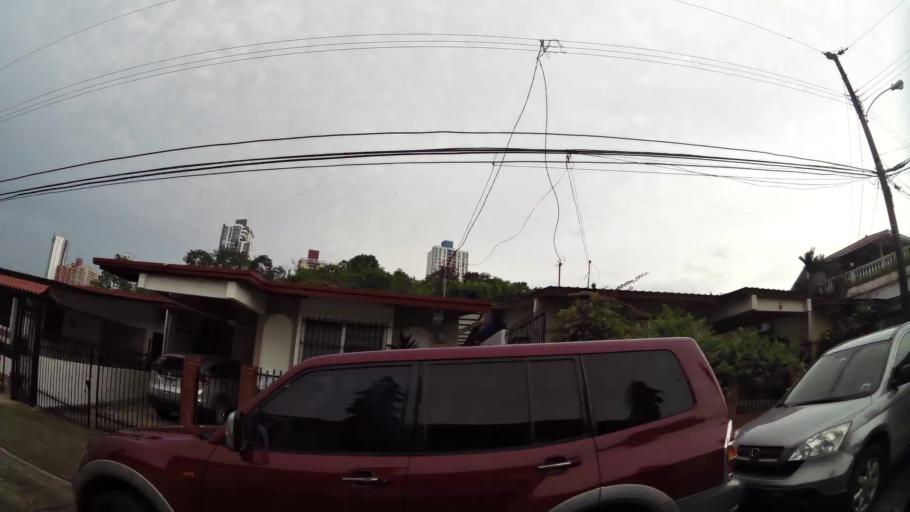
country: PA
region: Panama
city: Panama
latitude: 9.0134
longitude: -79.5371
